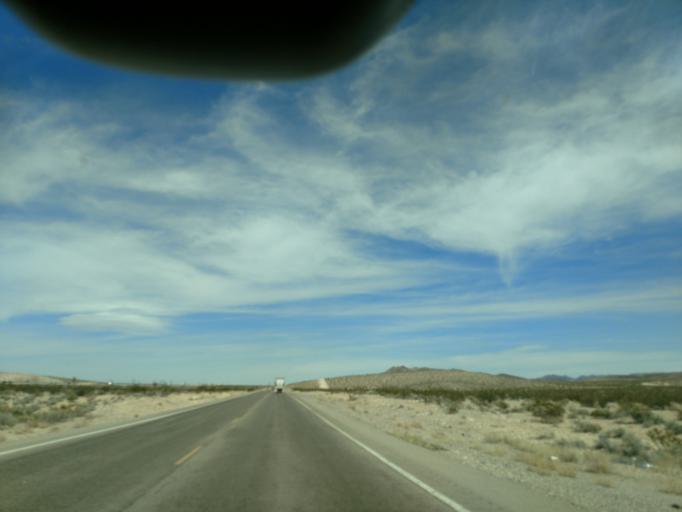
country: US
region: Nevada
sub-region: Clark County
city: Enterprise
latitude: 35.8602
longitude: -115.2509
